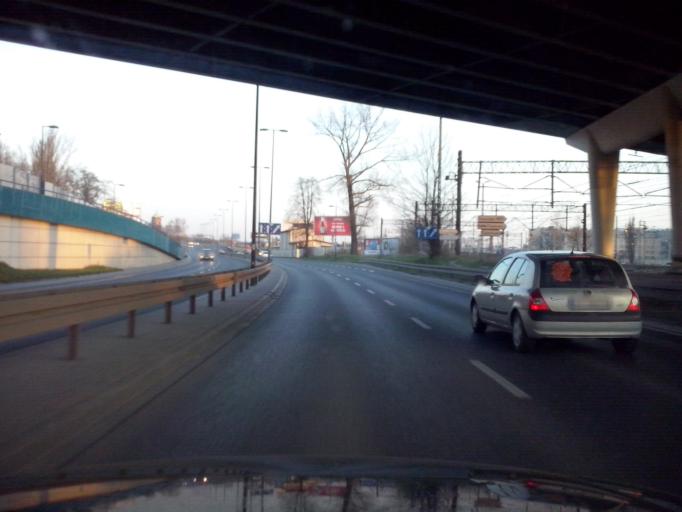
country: PL
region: Lesser Poland Voivodeship
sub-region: Krakow
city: Krakow
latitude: 50.0744
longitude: 19.9458
